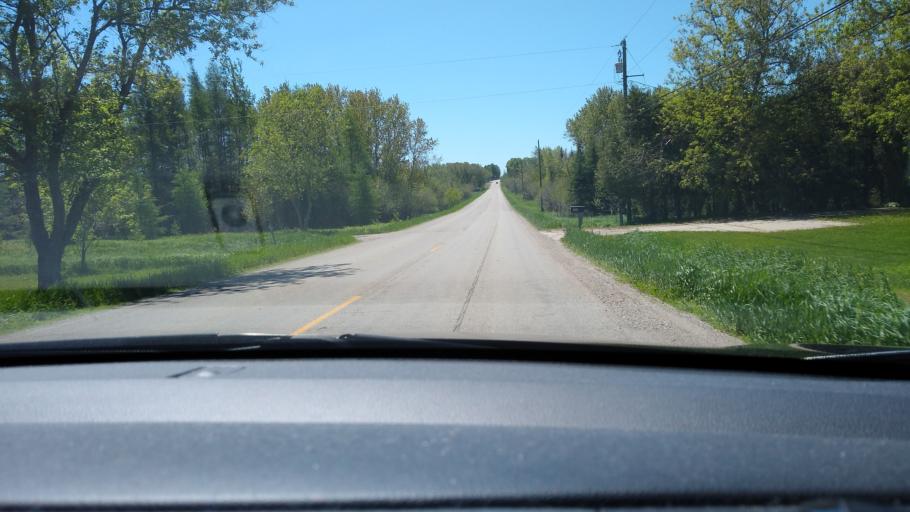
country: US
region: Michigan
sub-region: Delta County
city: Escanaba
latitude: 45.8330
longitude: -87.1835
